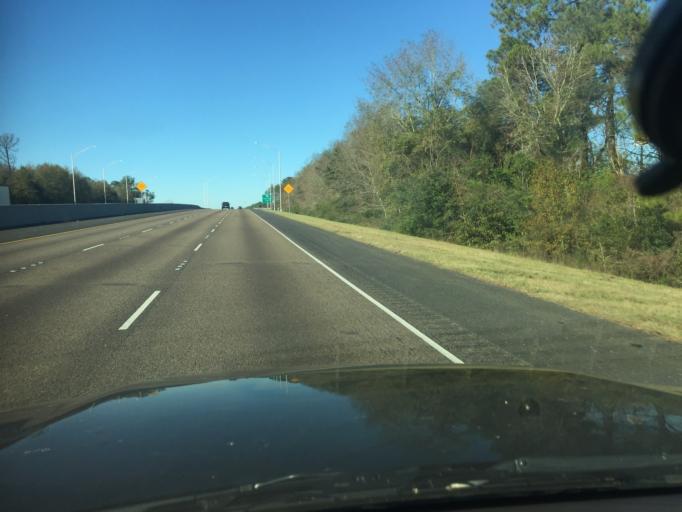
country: US
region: Louisiana
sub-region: Saint Tammany Parish
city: Slidell
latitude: 30.3103
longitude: -89.7666
